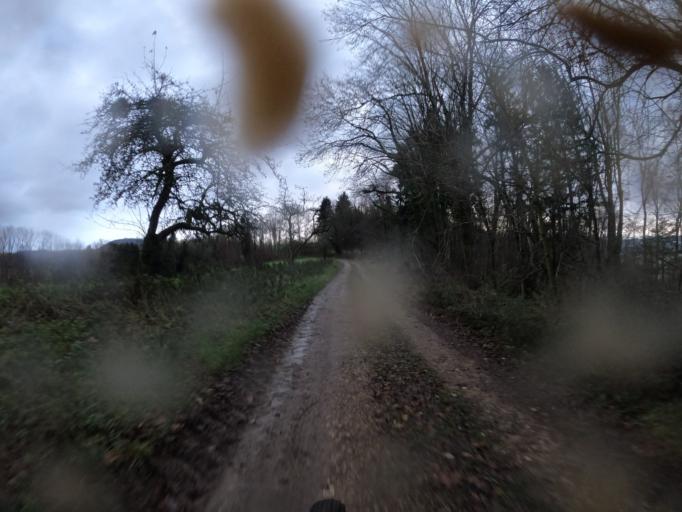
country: DE
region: Baden-Wuerttemberg
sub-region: Regierungsbezirk Stuttgart
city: Donzdorf
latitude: 48.6984
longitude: 9.7816
